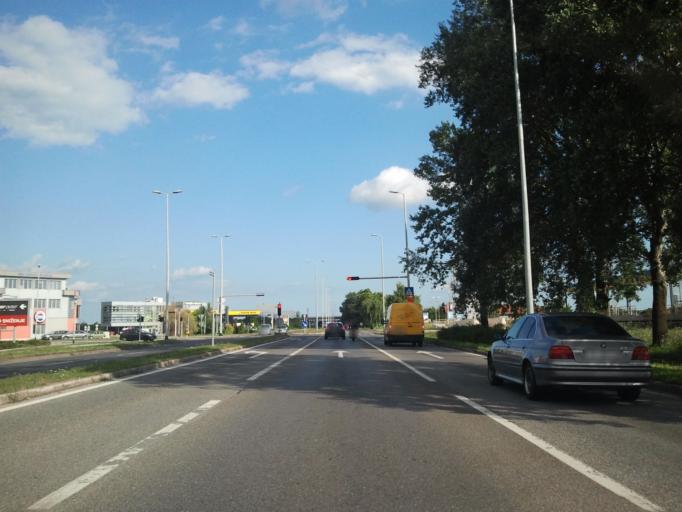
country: HR
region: Grad Zagreb
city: Odra
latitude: 45.7439
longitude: 15.9982
